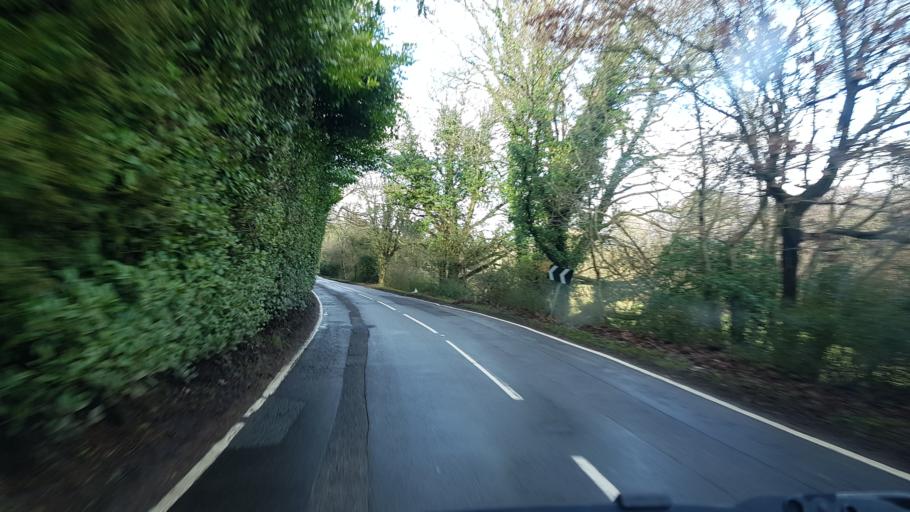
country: GB
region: England
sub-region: Surrey
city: Churt
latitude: 51.1712
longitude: -0.7489
